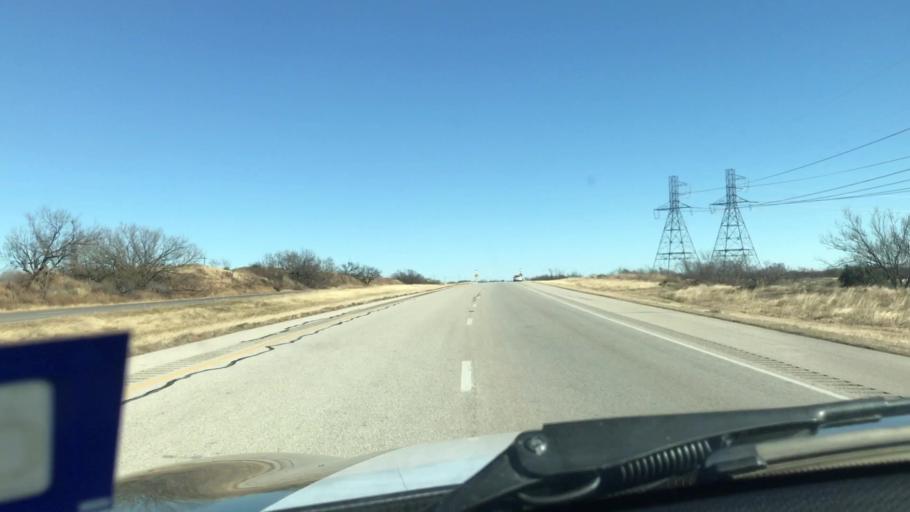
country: US
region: Texas
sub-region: Scurry County
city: Snyder
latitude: 32.6799
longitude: -100.8185
